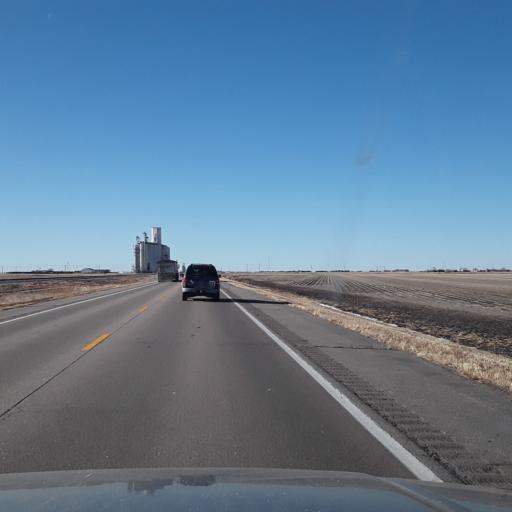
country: US
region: Nebraska
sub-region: Kearney County
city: Minden
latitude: 40.4934
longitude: -99.0178
